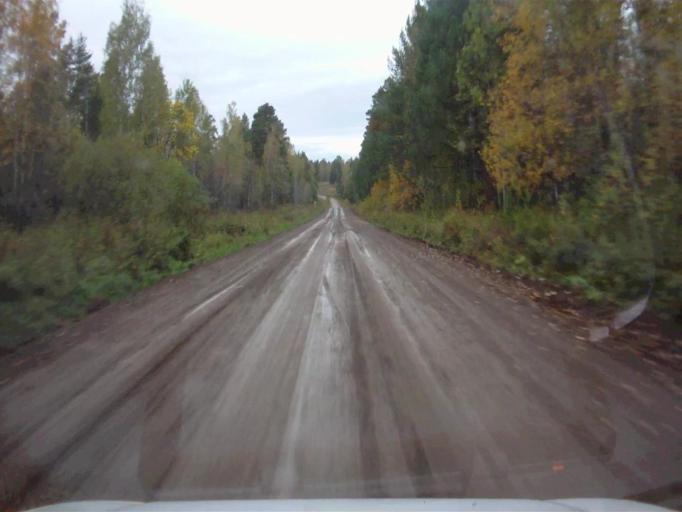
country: RU
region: Chelyabinsk
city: Nyazepetrovsk
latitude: 56.0878
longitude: 59.4168
